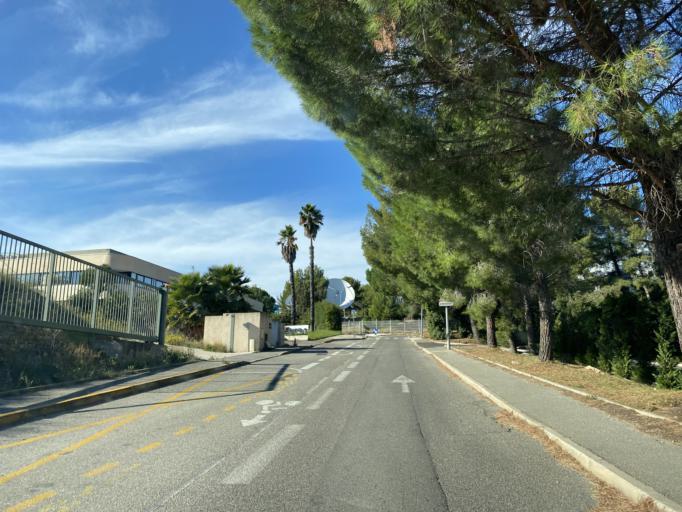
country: FR
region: Provence-Alpes-Cote d'Azur
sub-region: Departement des Bouches-du-Rhone
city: Ceyreste
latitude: 43.2073
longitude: 5.6081
